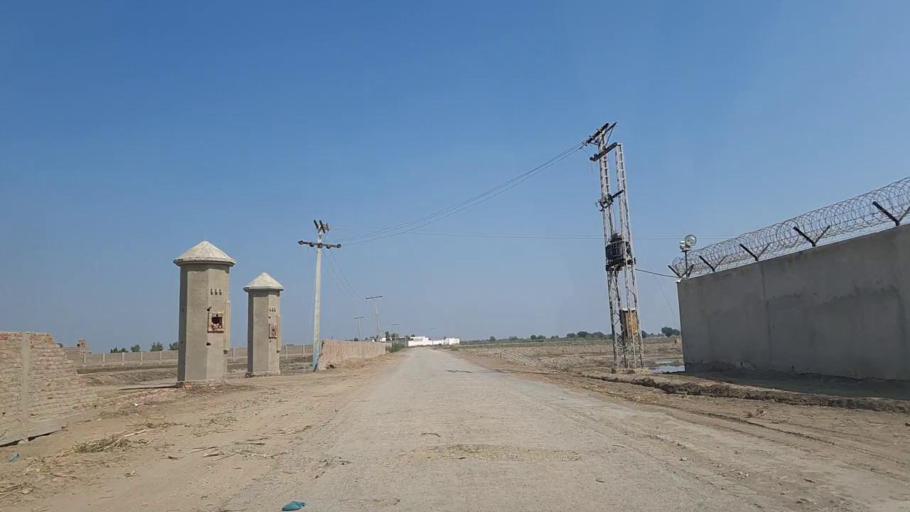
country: PK
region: Sindh
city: Digri
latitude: 25.1603
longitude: 69.1196
